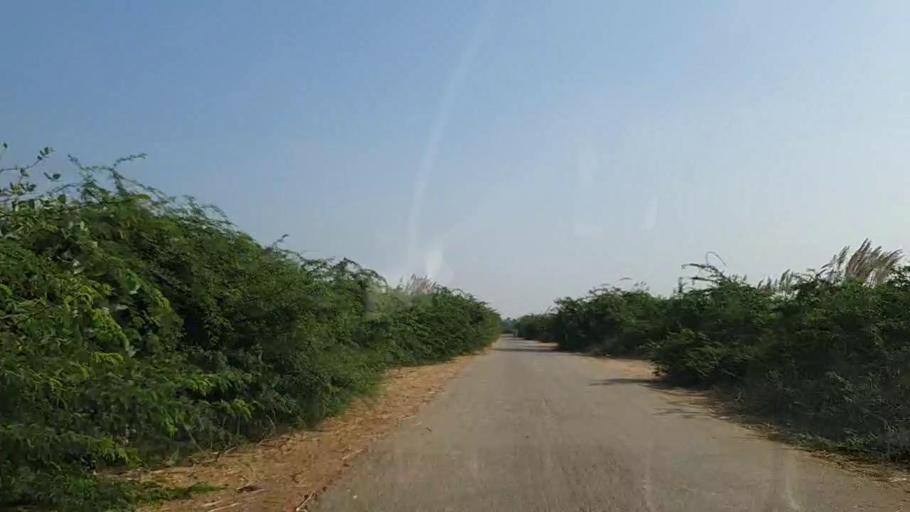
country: PK
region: Sindh
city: Mirpur Sakro
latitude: 24.6215
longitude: 67.6584
